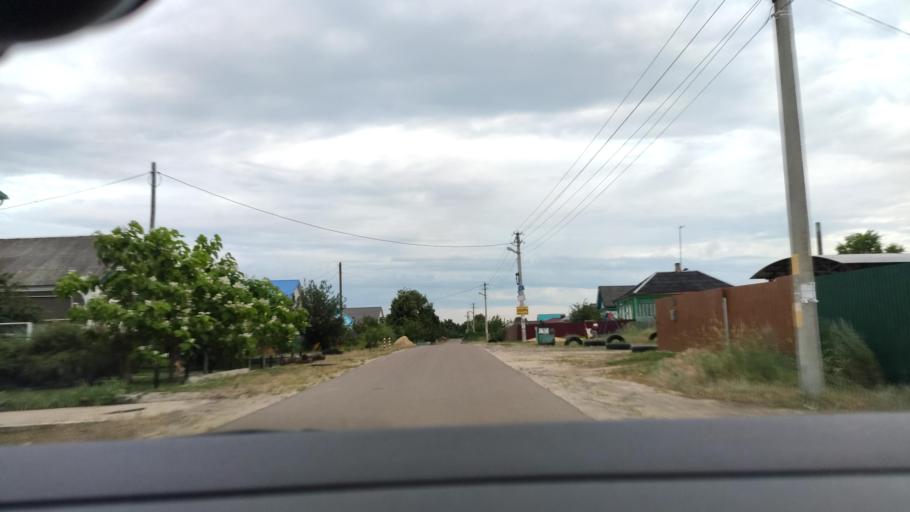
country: RU
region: Voronezj
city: Maslovka
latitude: 51.5679
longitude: 39.2501
